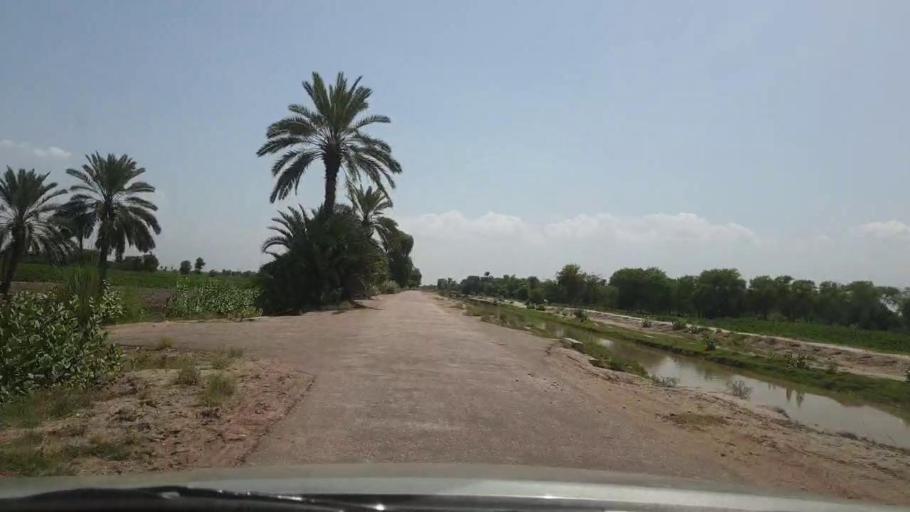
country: PK
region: Sindh
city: Pano Aqil
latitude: 27.7309
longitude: 69.0934
